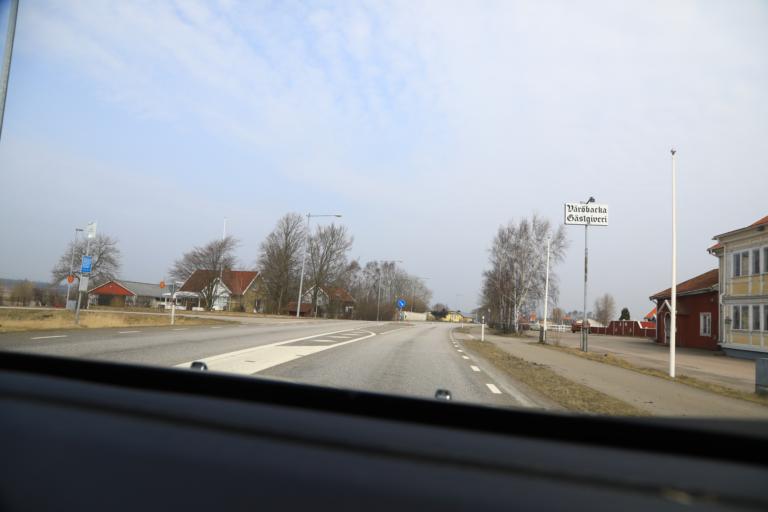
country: SE
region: Halland
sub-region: Kungsbacka Kommun
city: Frillesas
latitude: 57.2527
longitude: 12.1814
